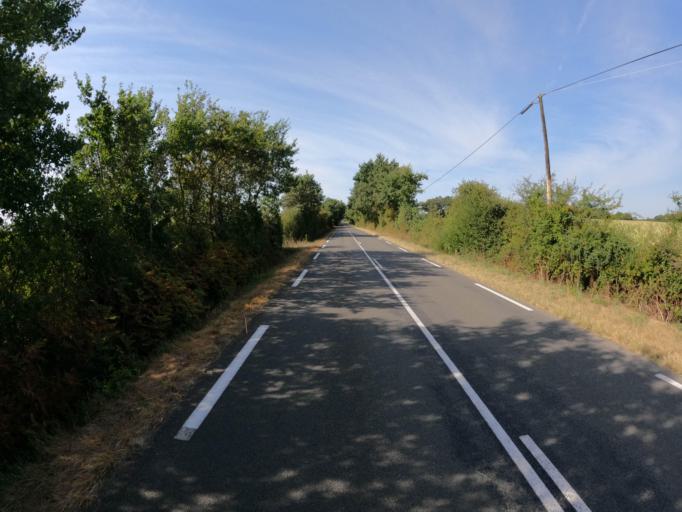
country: FR
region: Pays de la Loire
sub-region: Departement de la Vendee
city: Falleron
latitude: 46.8651
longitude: -1.7081
